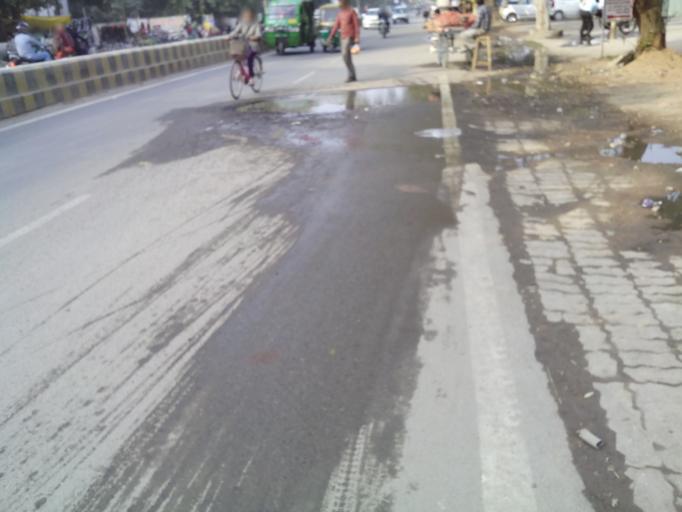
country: IN
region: Uttar Pradesh
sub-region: Kanpur
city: Kanpur
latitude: 26.4345
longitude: 80.3086
